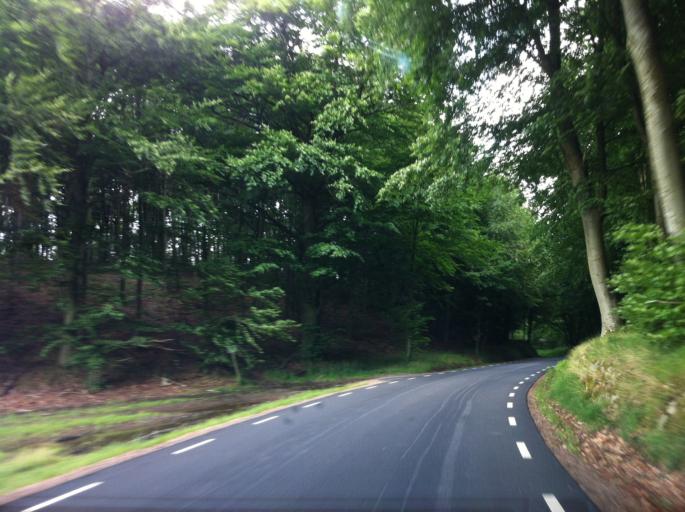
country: SE
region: Skane
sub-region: Trelleborgs Kommun
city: Anderslov
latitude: 55.4731
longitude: 13.3659
